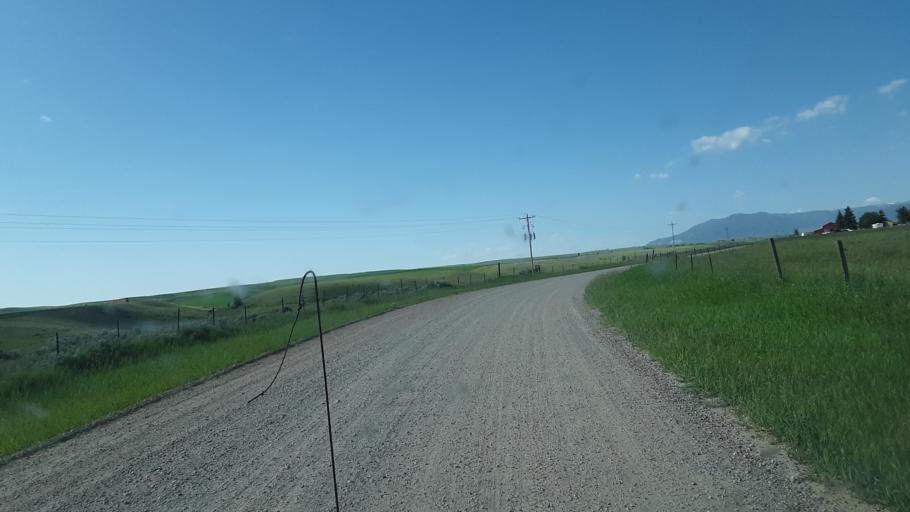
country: US
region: Montana
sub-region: Carbon County
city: Red Lodge
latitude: 45.3397
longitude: -109.1611
